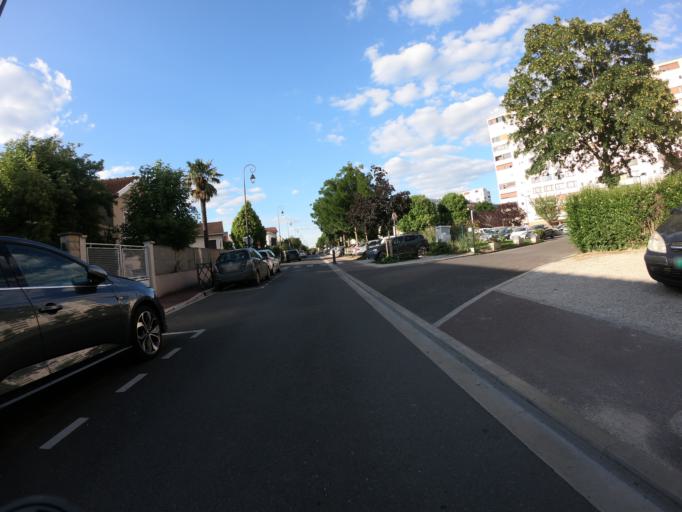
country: FR
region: Ile-de-France
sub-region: Departement du Val-de-Marne
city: Fresnes
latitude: 48.7575
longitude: 2.3108
